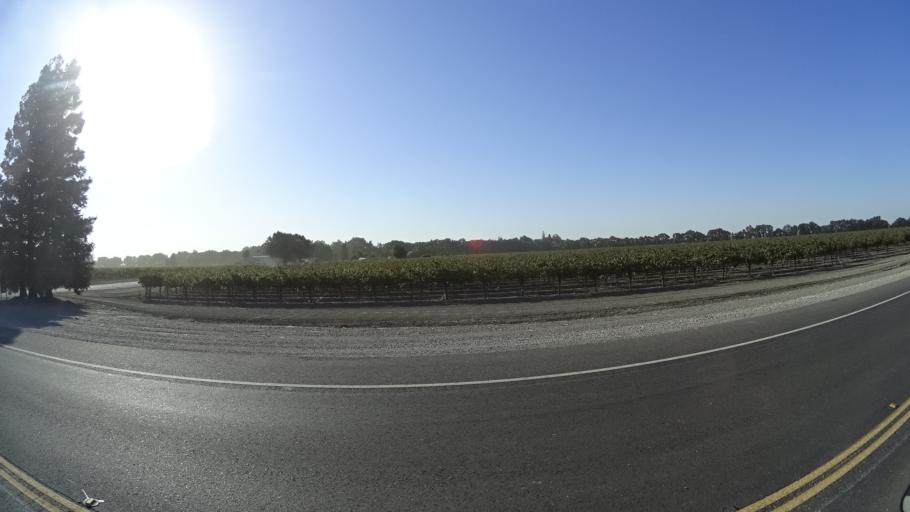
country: US
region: California
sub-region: Sacramento County
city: Parkway
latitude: 38.4147
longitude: -121.5430
